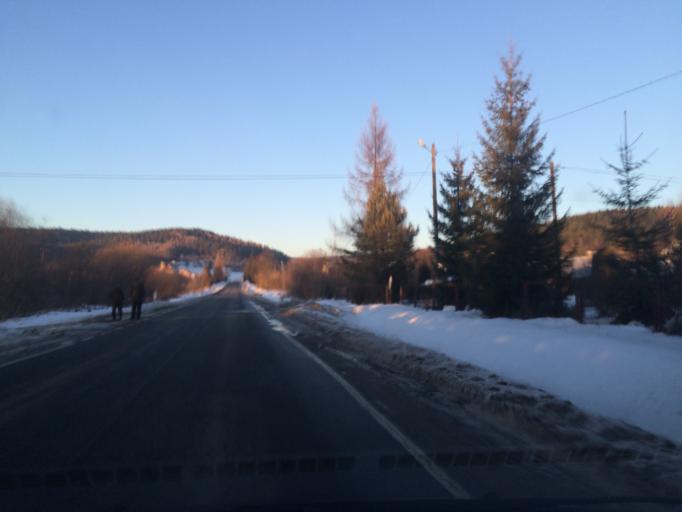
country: PL
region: Subcarpathian Voivodeship
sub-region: Powiat bieszczadzki
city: Czarna
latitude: 49.3338
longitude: 22.6716
